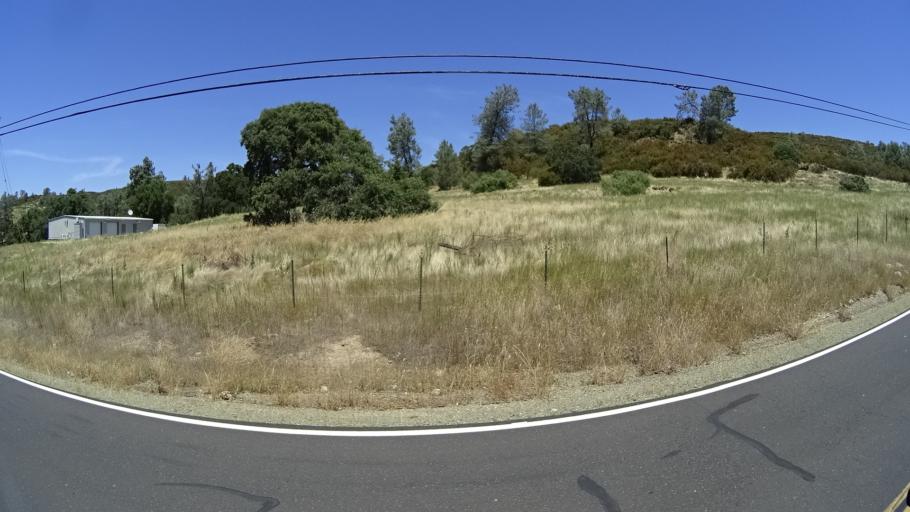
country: US
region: California
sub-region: Calaveras County
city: Valley Springs
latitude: 38.2330
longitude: -120.8072
